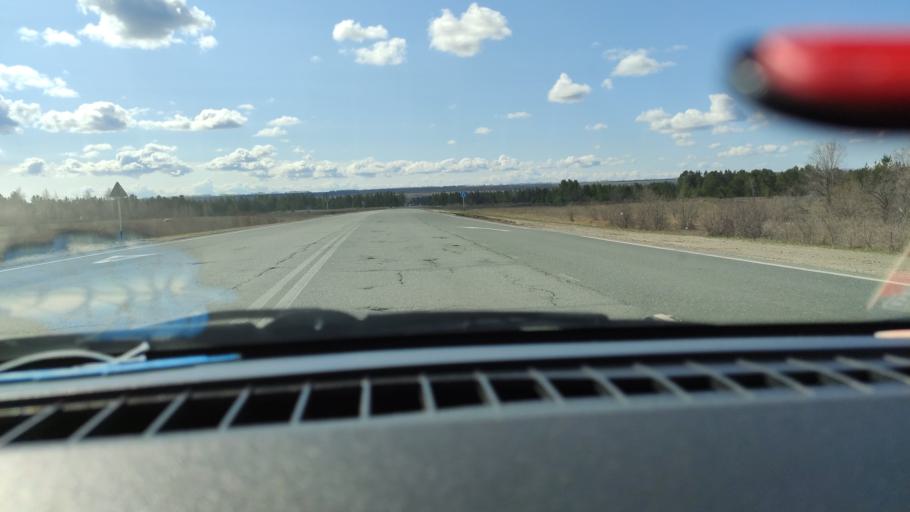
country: RU
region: Samara
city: Varlamovo
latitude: 53.1505
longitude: 48.2842
